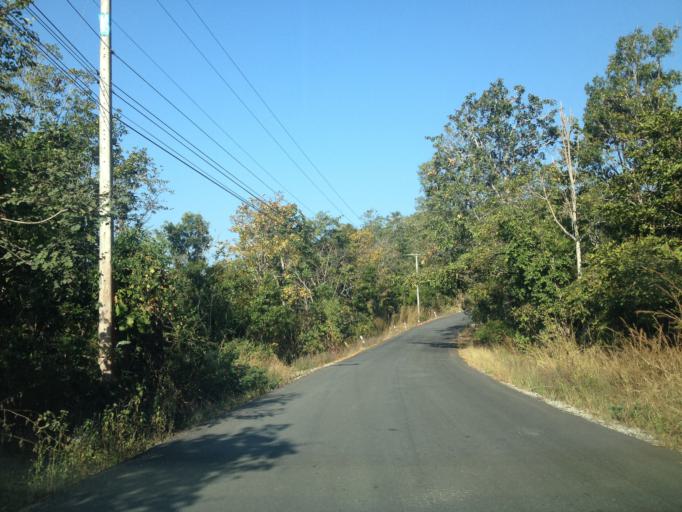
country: TH
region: Mae Hong Son
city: Ban Huai I Huak
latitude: 18.1365
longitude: 98.2197
